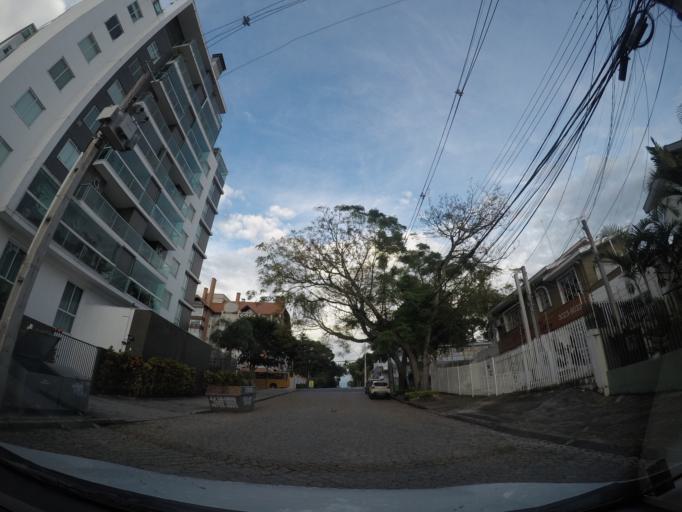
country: BR
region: Parana
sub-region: Curitiba
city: Curitiba
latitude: -25.4249
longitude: -49.2874
